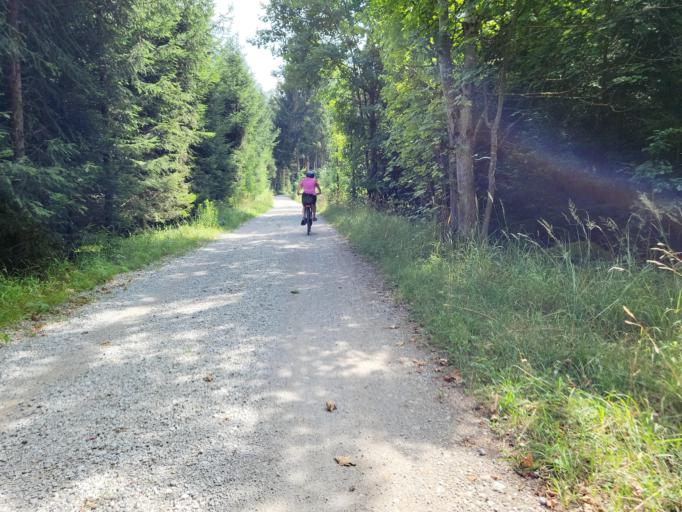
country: DE
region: Bavaria
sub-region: Upper Bavaria
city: Putzbrunn
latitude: 48.0568
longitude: 11.7222
